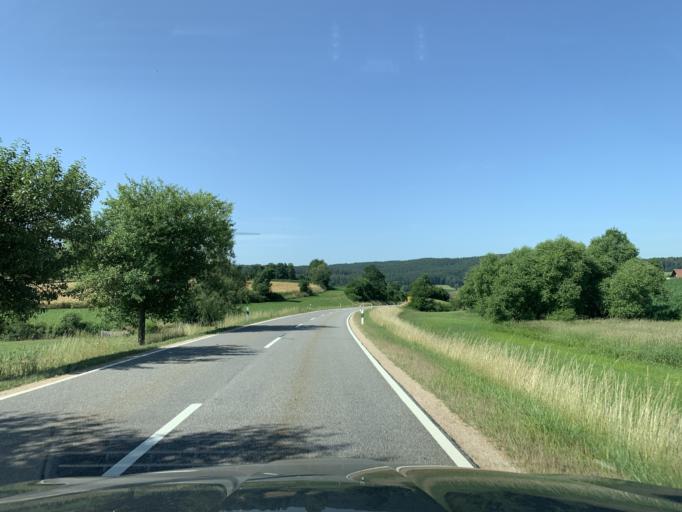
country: DE
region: Bavaria
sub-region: Upper Palatinate
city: Schwarzhofen
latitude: 49.3824
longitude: 12.3480
